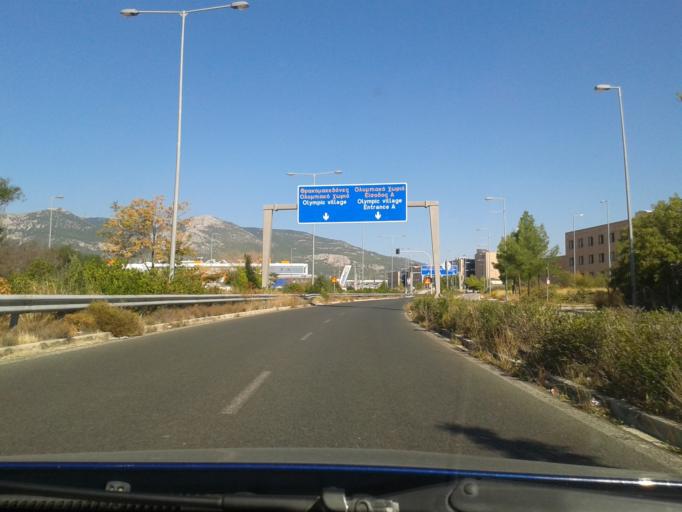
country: GR
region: Attica
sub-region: Nomarchia Anatolikis Attikis
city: Thrakomakedones
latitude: 38.1030
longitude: 23.7642
